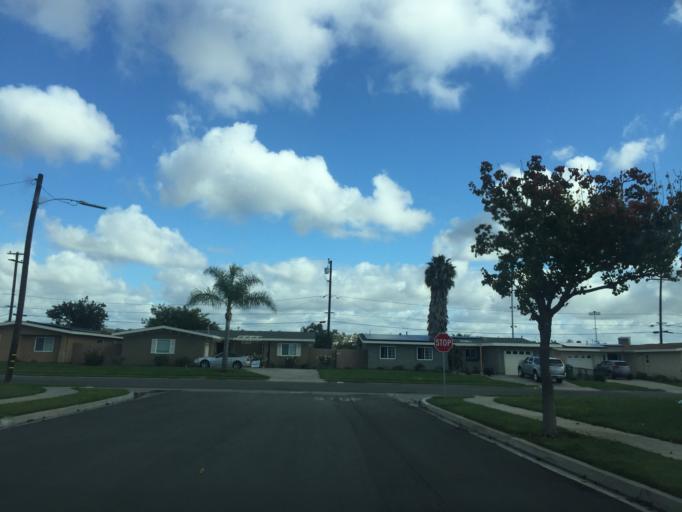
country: US
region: California
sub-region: San Diego County
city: La Jolla
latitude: 32.7989
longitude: -117.2267
